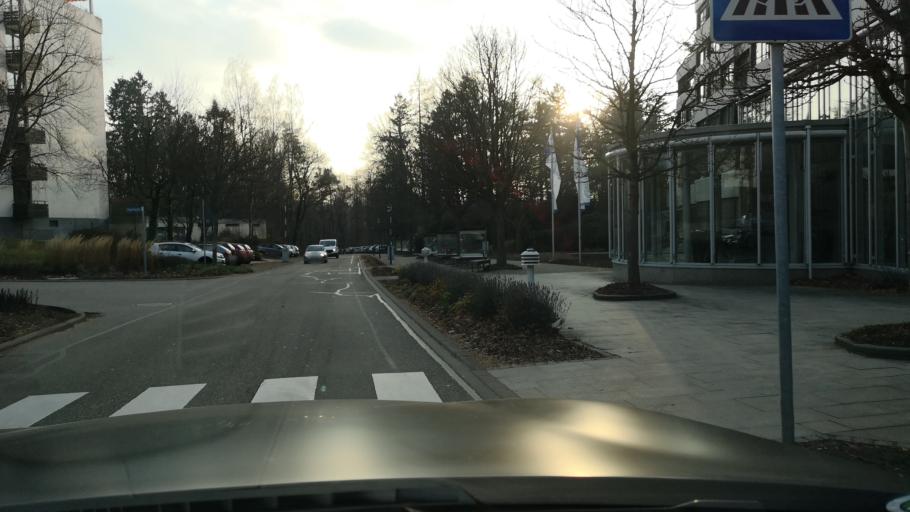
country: DE
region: Baden-Wuerttemberg
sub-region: Karlsruhe Region
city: Ettlingen
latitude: 48.9258
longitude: 8.4708
